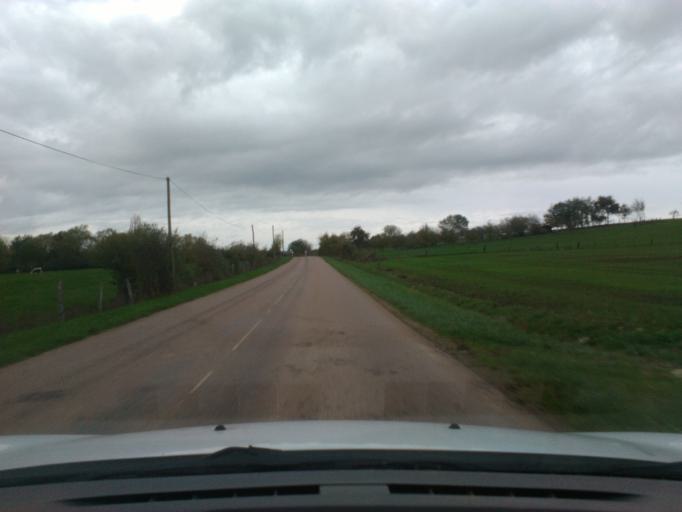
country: FR
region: Lorraine
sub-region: Departement des Vosges
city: Mirecourt
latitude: 48.3501
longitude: 6.0930
